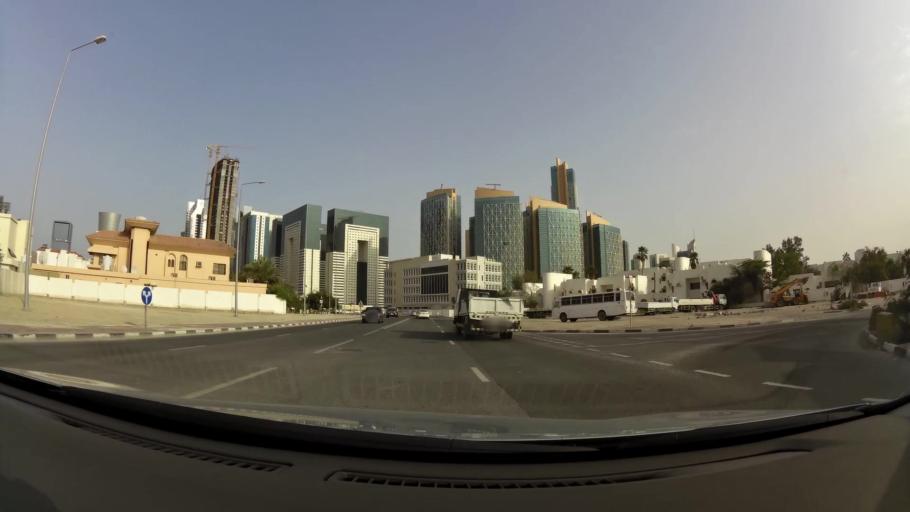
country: QA
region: Baladiyat ad Dawhah
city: Doha
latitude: 25.3209
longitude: 51.5157
